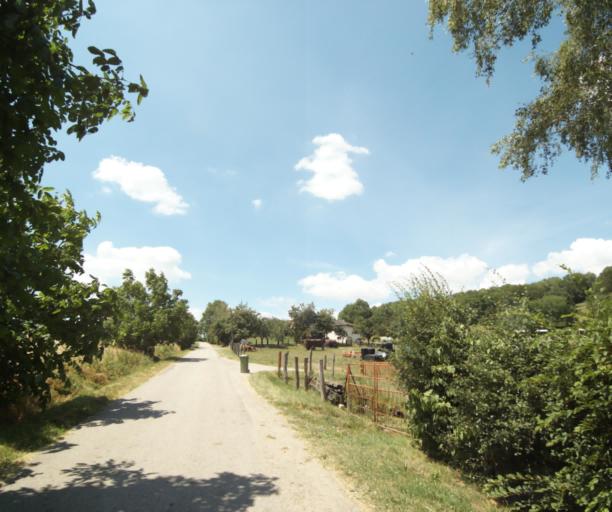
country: FR
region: Lorraine
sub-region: Departement de Meurthe-et-Moselle
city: Luneville
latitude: 48.6030
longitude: 6.4592
